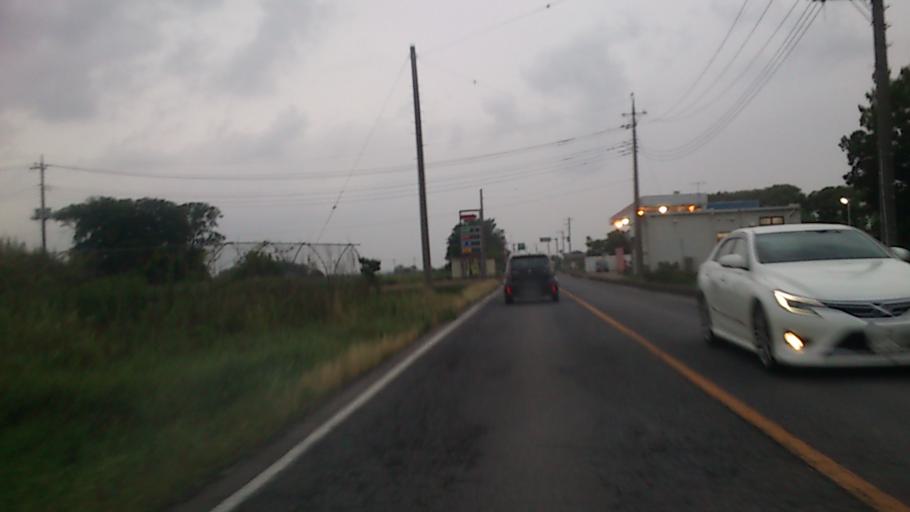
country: JP
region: Saitama
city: Kazo
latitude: 36.1590
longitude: 139.6088
